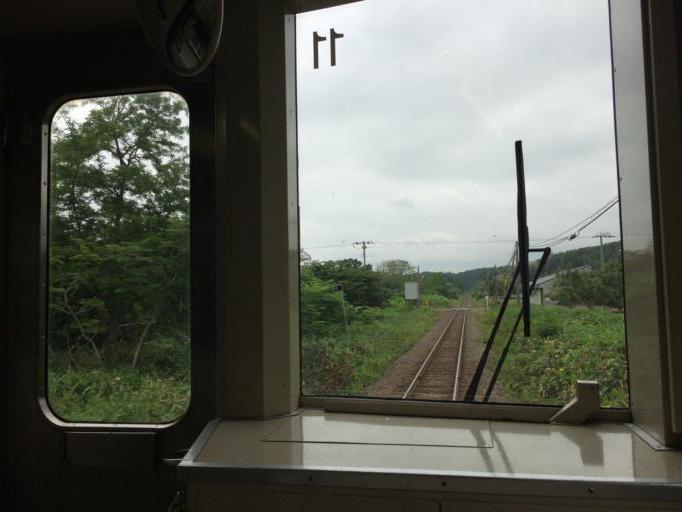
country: JP
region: Hokkaido
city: Yoichi
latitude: 43.1930
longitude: 140.8289
